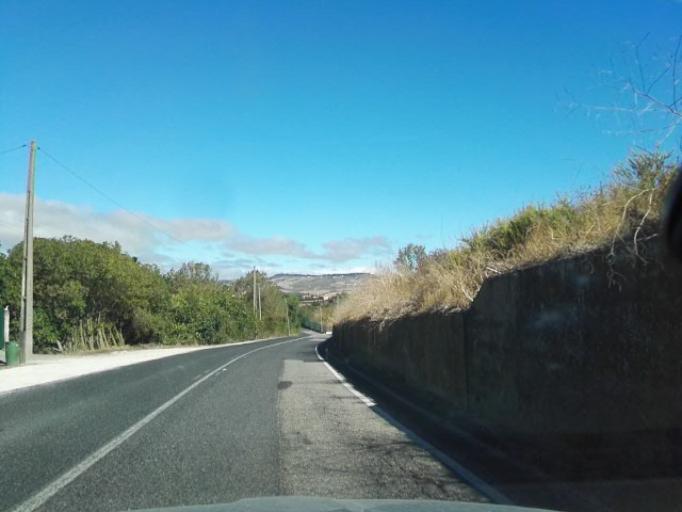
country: PT
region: Lisbon
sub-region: Arruda Dos Vinhos
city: Arruda dos Vinhos
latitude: 38.9661
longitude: -9.0638
